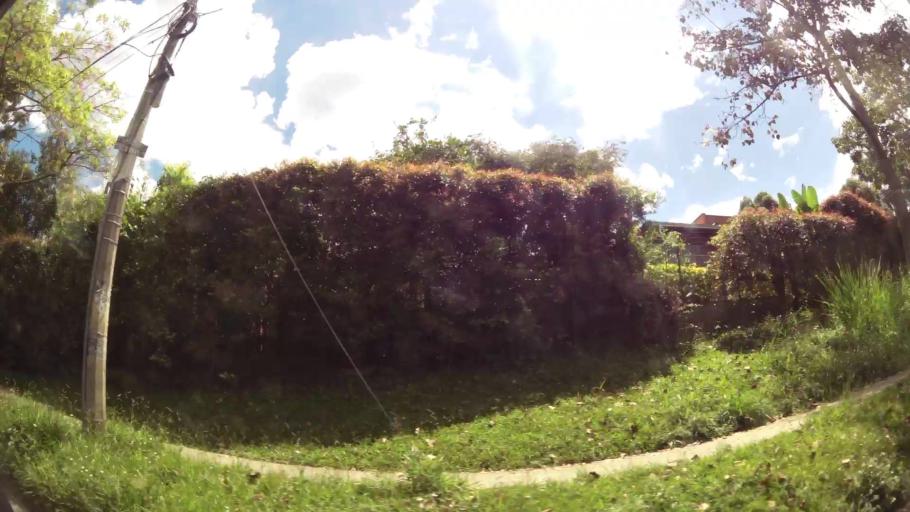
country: CO
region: Antioquia
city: Sabaneta
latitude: 6.1582
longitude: -75.6283
